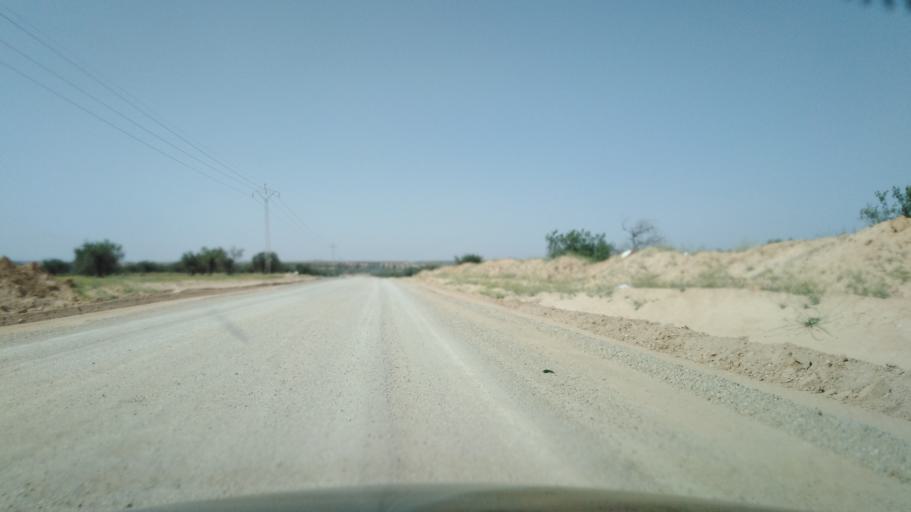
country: TN
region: Safaqis
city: Sfax
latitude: 34.6993
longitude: 10.4822
